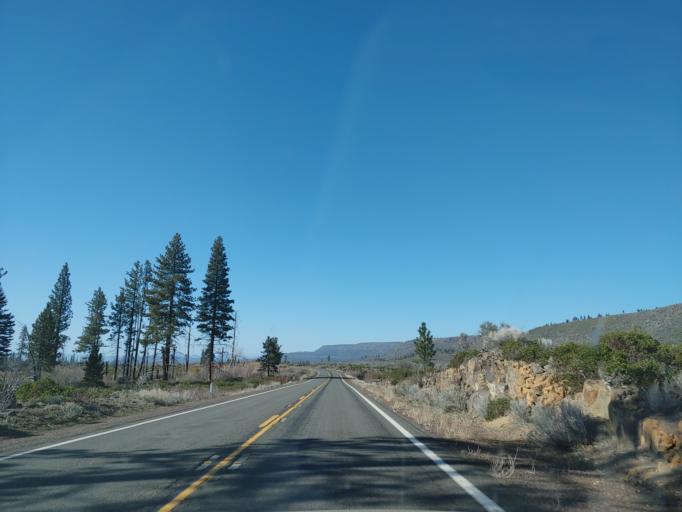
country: US
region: California
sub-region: Shasta County
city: Burney
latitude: 40.7017
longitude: -121.4179
